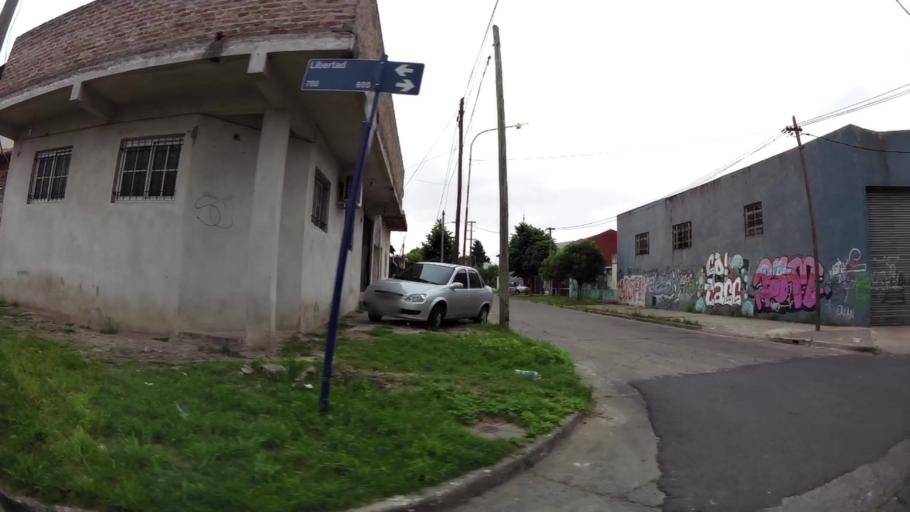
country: AR
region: Buenos Aires F.D.
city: Villa Lugano
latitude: -34.7089
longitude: -58.5117
